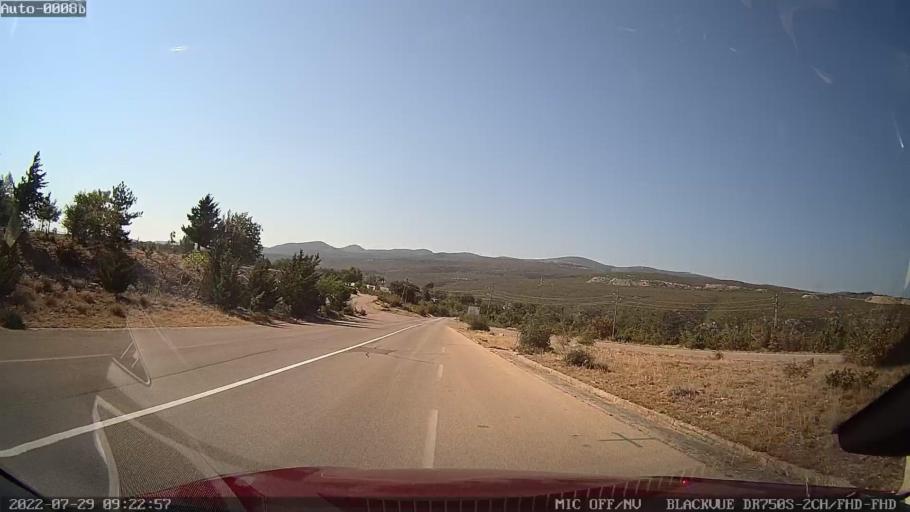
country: HR
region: Zadarska
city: Obrovac
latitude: 44.2108
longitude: 15.6684
